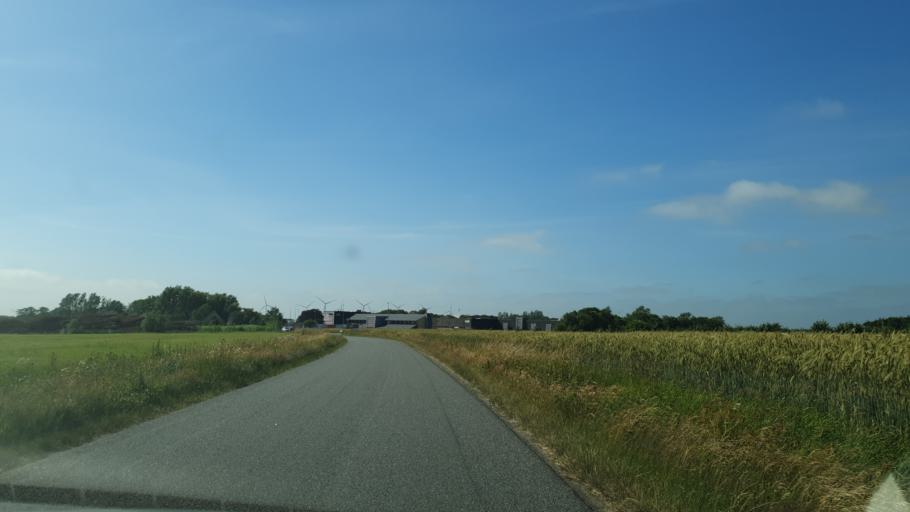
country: DK
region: Central Jutland
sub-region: Ringkobing-Skjern Kommune
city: Skjern
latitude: 56.0246
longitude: 8.4031
